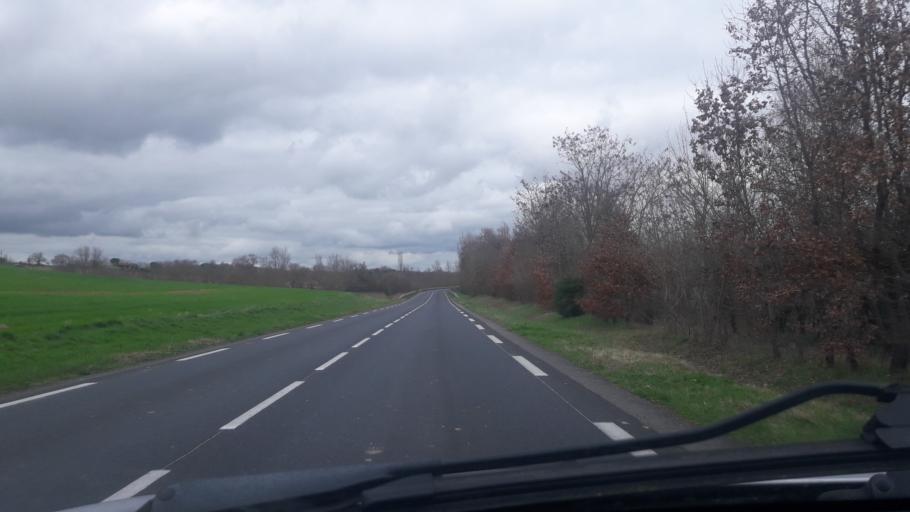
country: FR
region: Midi-Pyrenees
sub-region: Departement du Gers
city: Pujaudran
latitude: 43.6176
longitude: 1.0665
